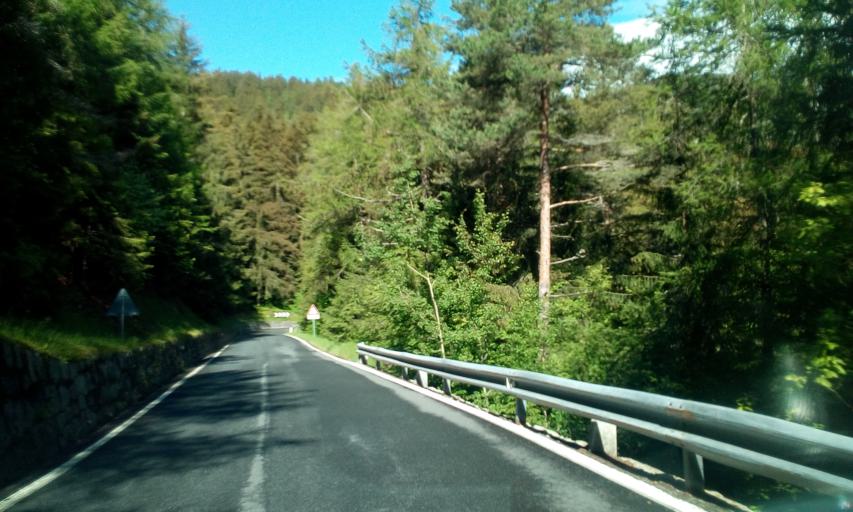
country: IT
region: Aosta Valley
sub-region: Valle d'Aosta
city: Brusson
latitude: 45.7551
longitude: 7.7195
